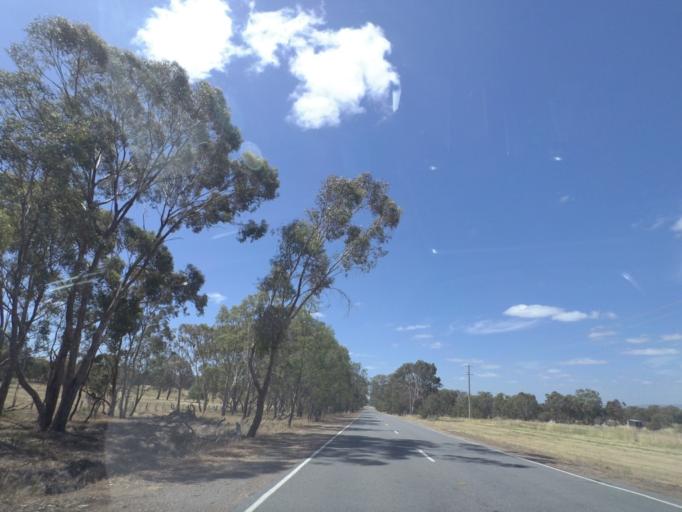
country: AU
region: Victoria
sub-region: Wangaratta
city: Wangaratta
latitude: -36.4479
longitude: 146.2403
